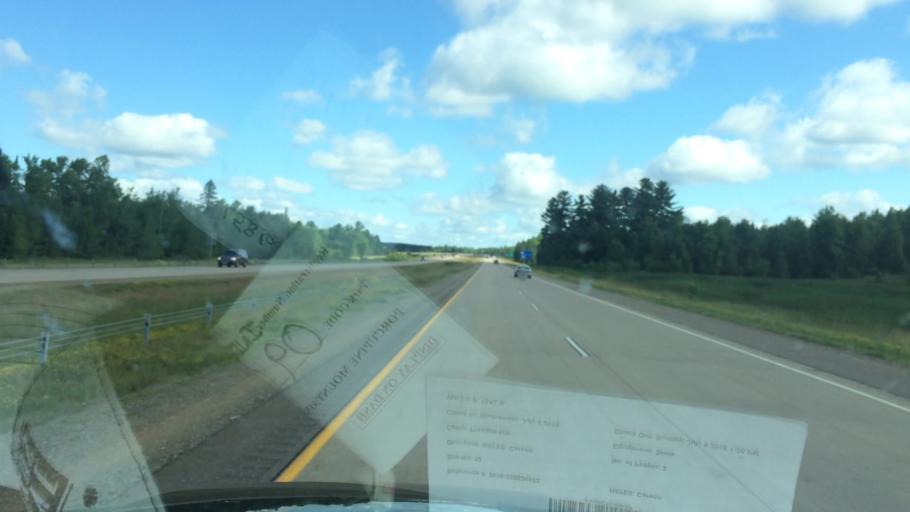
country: US
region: Wisconsin
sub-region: Lincoln County
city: Tomahawk
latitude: 45.4068
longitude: -89.6717
